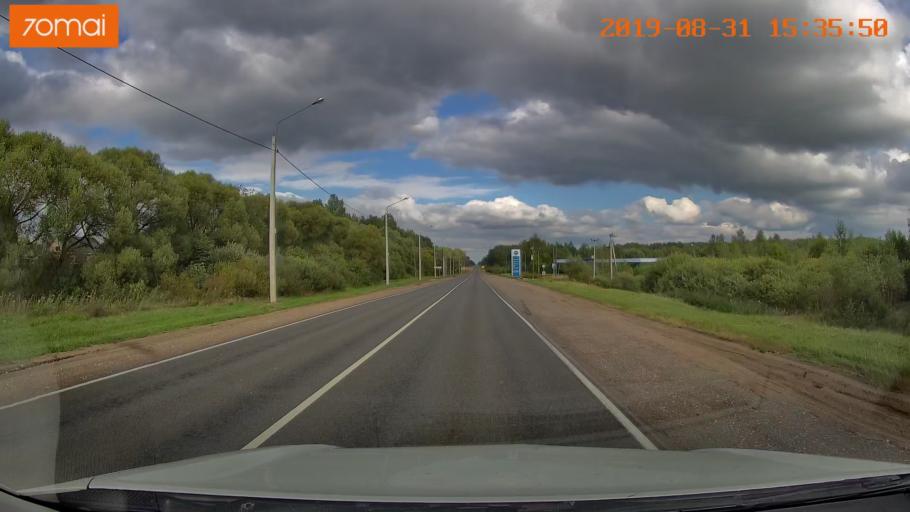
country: RU
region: Kaluga
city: Mosal'sk
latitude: 54.6075
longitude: 34.7454
